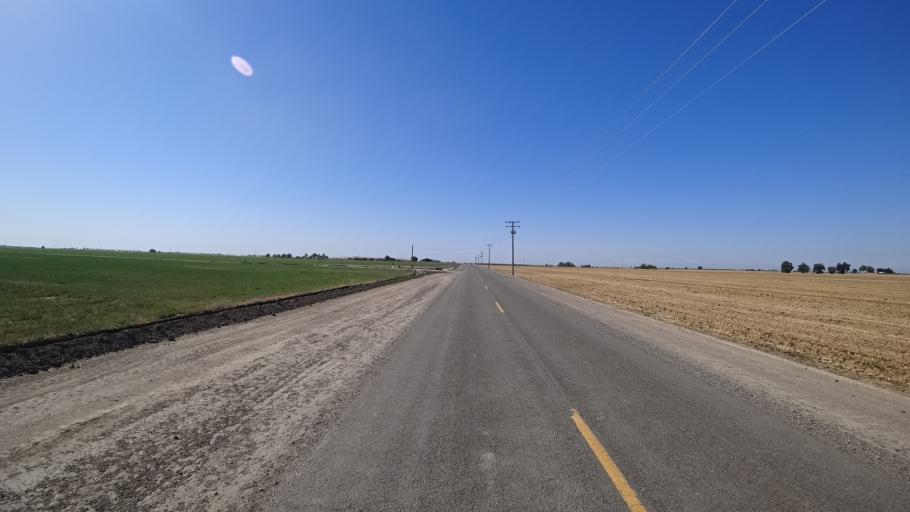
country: US
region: California
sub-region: Kings County
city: Home Garden
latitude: 36.2316
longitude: -119.5562
